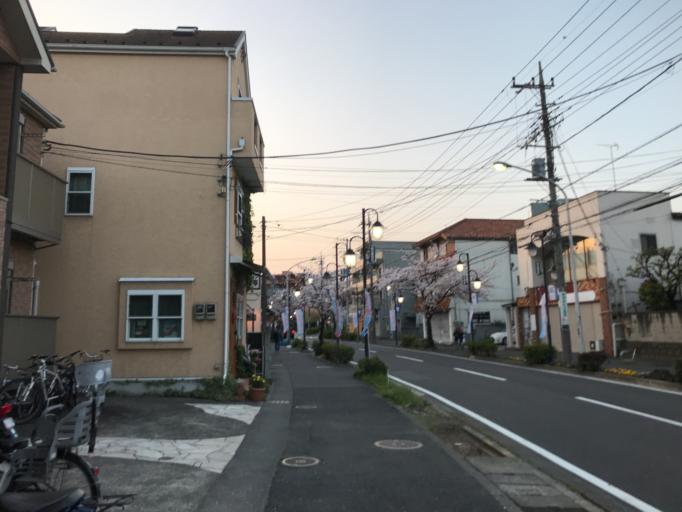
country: JP
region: Tokyo
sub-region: Machida-shi
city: Machida
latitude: 35.5507
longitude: 139.5145
